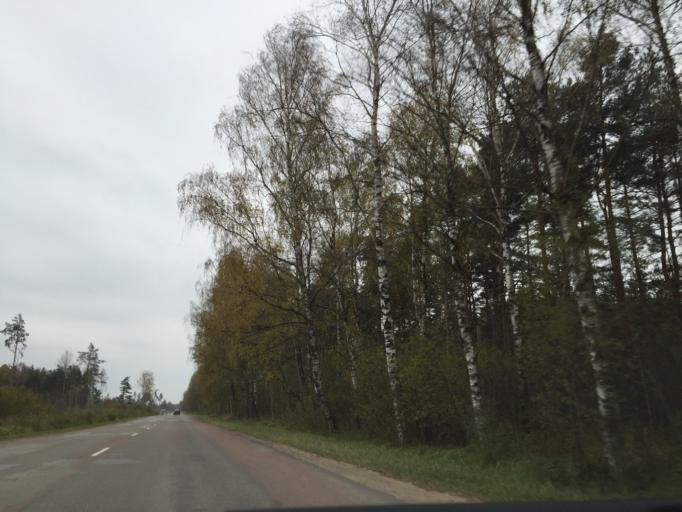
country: LV
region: Marupe
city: Marupe
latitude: 56.8679
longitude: 24.0622
